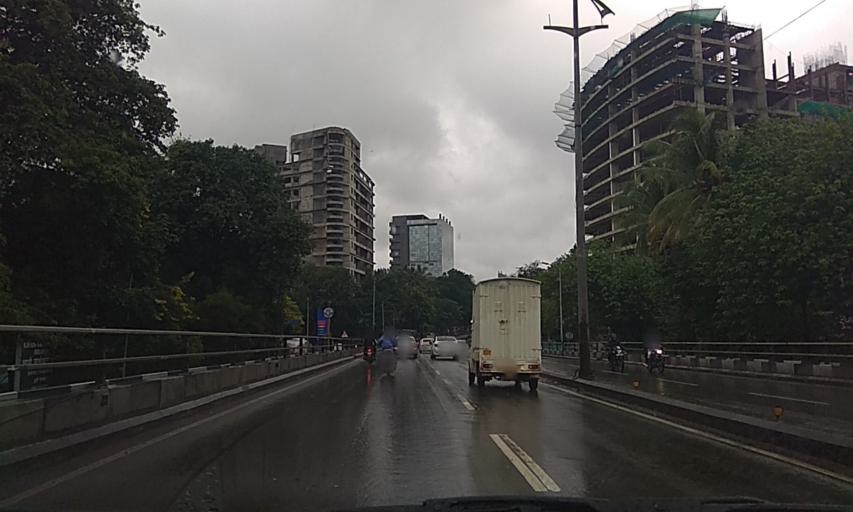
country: IN
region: Maharashtra
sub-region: Pune Division
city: Shivaji Nagar
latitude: 18.5315
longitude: 73.8443
